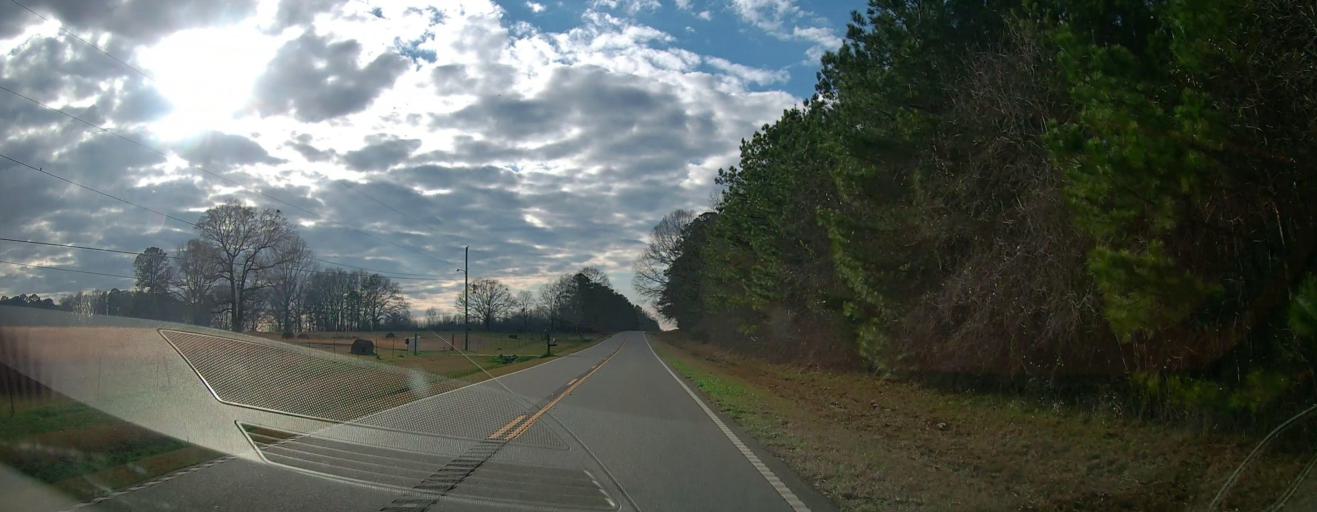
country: US
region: Georgia
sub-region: Harris County
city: Hamilton
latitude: 32.6850
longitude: -84.7648
